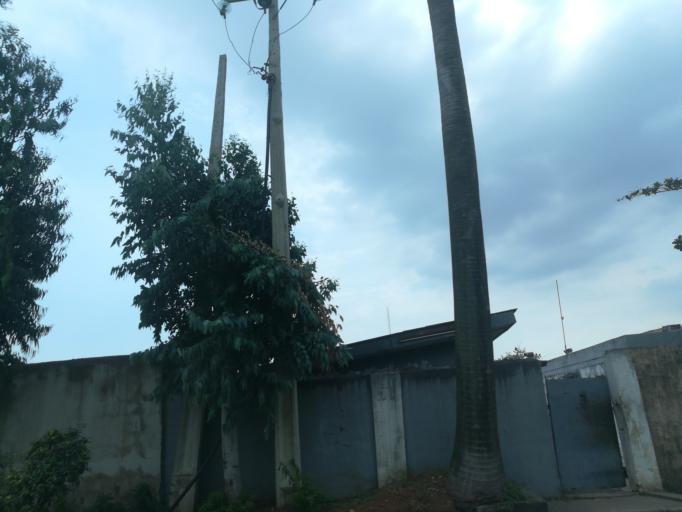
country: NG
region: Lagos
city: Ikeja
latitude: 6.6095
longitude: 3.3606
